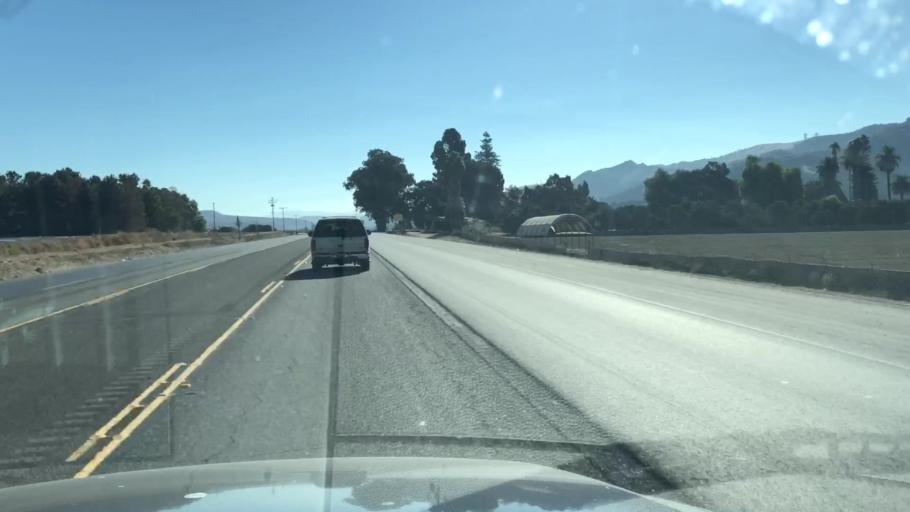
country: US
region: California
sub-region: Ventura County
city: Piru
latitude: 34.4070
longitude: -118.7594
